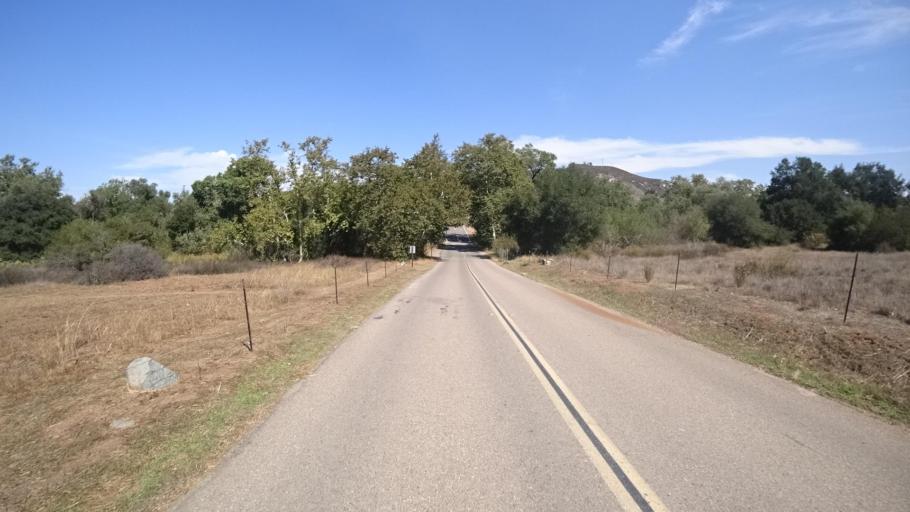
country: US
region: California
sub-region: San Diego County
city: Rancho San Diego
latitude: 32.7299
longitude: -116.9394
